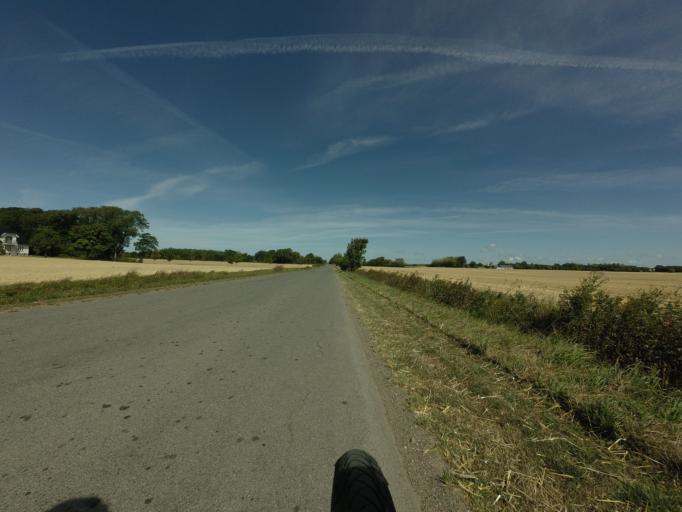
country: DK
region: North Denmark
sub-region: Bronderslev Kommune
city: Bronderslev
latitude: 57.3248
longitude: 9.8204
